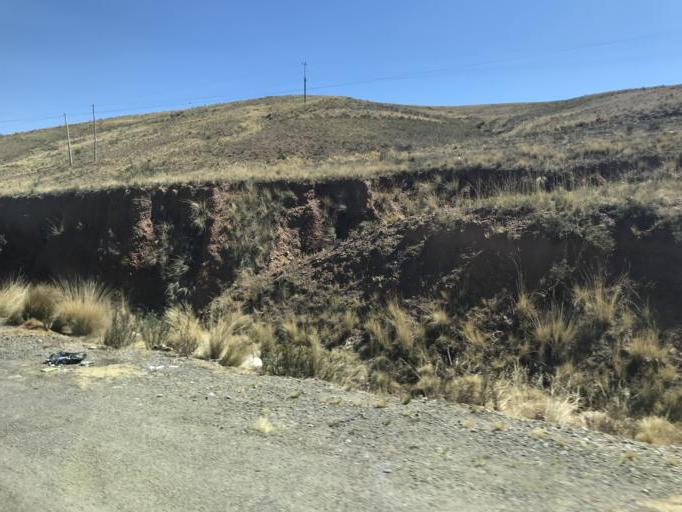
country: BO
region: La Paz
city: Tiahuanaco
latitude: -16.5780
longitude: -68.5378
